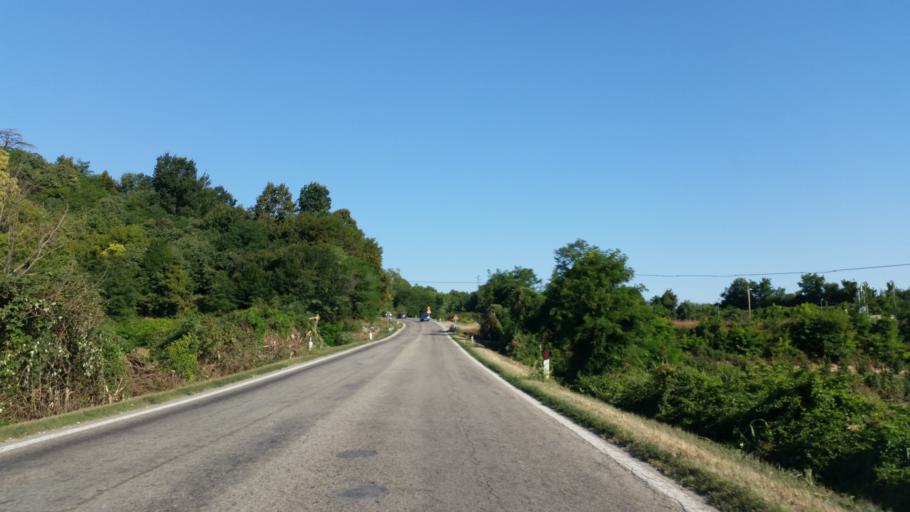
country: IT
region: Piedmont
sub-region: Provincia di Cuneo
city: Roreto
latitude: 44.6692
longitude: 7.8482
